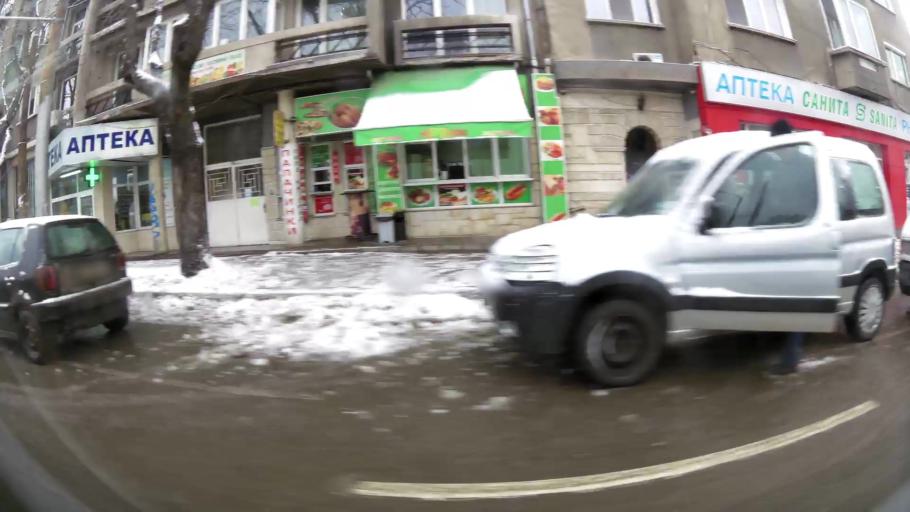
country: BG
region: Sofia-Capital
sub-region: Stolichna Obshtina
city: Sofia
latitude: 42.6861
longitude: 23.3071
